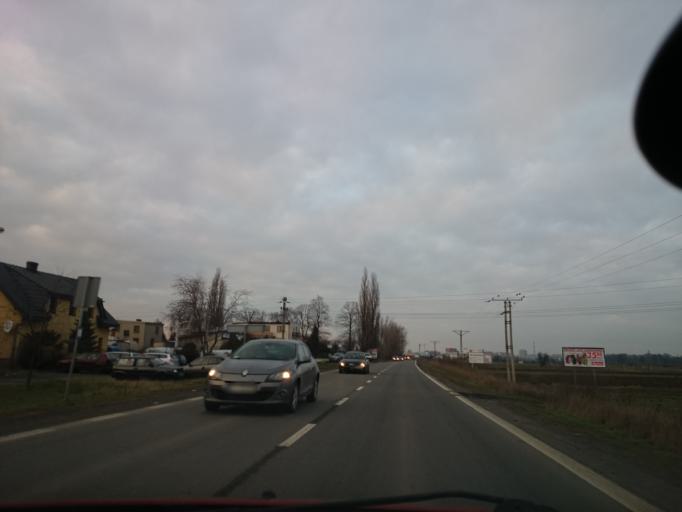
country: PL
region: Opole Voivodeship
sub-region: Powiat opolski
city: Opole
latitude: 50.6458
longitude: 17.9108
